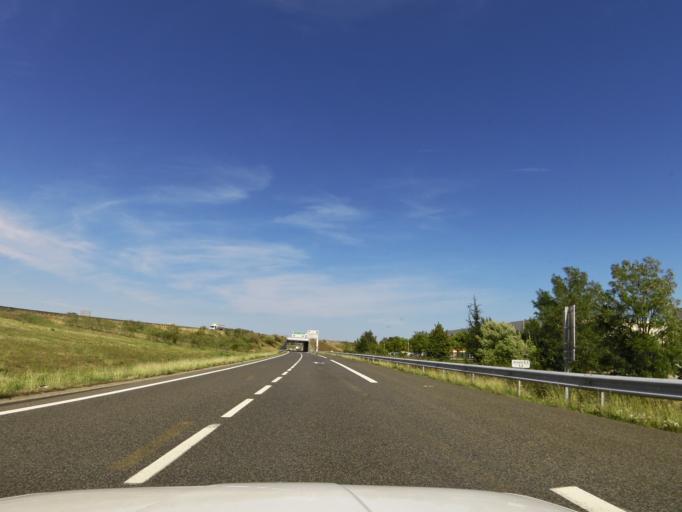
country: FR
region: Rhone-Alpes
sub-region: Departement du Rhone
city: Saint-Laurent-de-Mure
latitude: 45.6892
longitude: 5.0621
